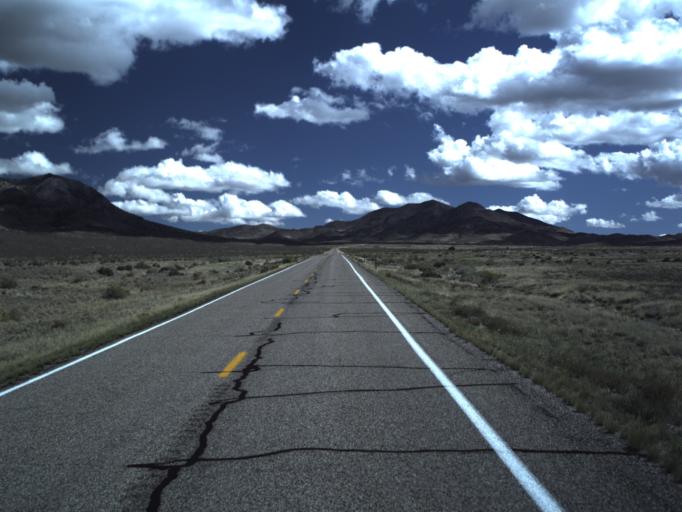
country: US
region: Utah
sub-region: Beaver County
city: Milford
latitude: 38.4514
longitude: -113.3485
